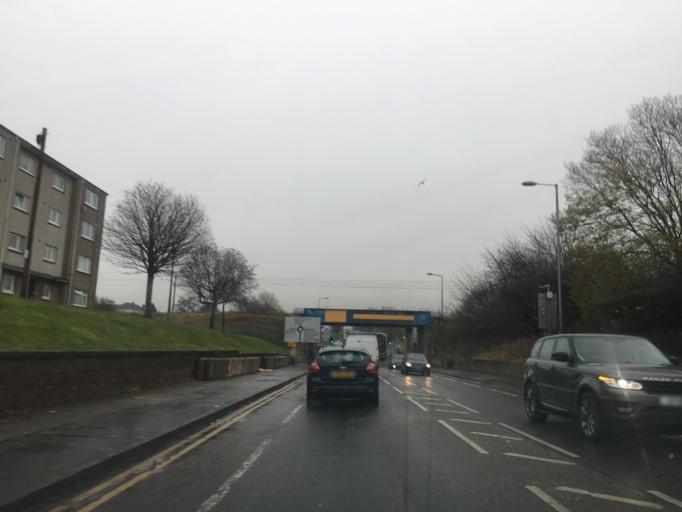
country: GB
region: Scotland
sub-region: Edinburgh
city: Colinton
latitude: 55.9312
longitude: -3.2863
